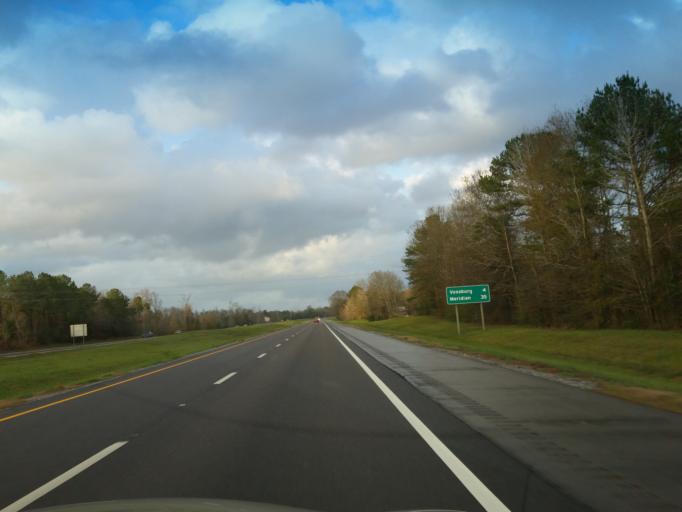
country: US
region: Mississippi
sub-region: Jones County
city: Sharon
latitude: 31.9147
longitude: -89.0066
